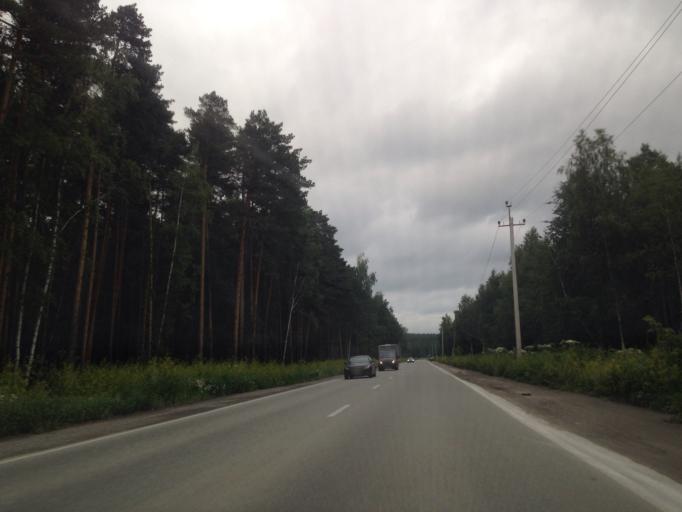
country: RU
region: Sverdlovsk
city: Istok
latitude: 56.8449
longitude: 60.7075
